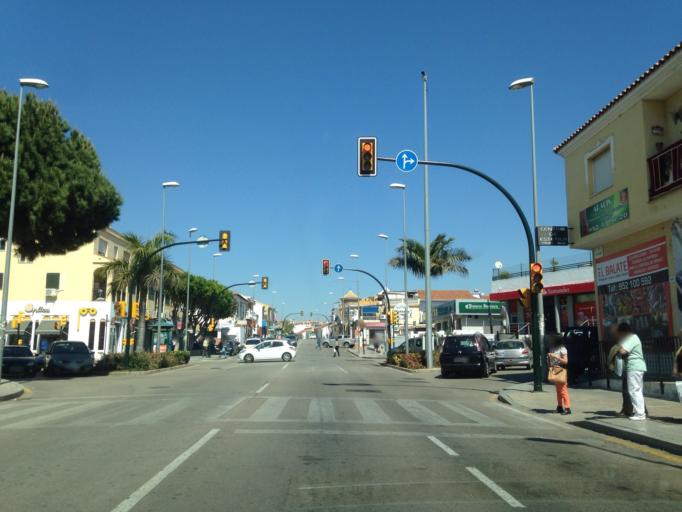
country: ES
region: Andalusia
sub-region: Provincia de Malaga
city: Malaga
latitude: 36.7380
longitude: -4.4805
